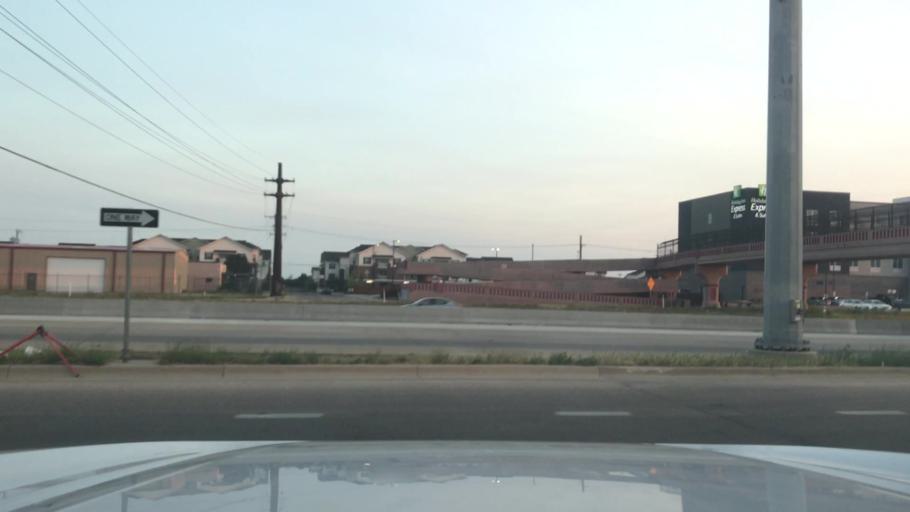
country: US
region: Texas
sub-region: Lubbock County
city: Lubbock
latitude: 33.5931
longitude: -101.8620
